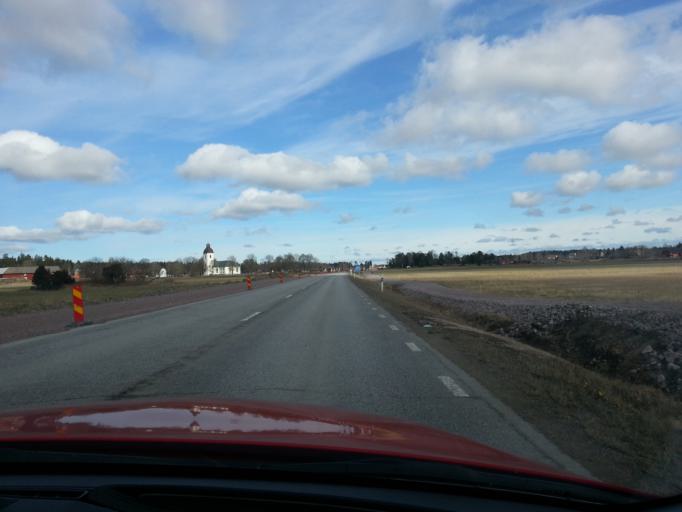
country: SE
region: Uppsala
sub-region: Osthammars Kommun
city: Gimo
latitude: 60.0556
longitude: 18.0618
